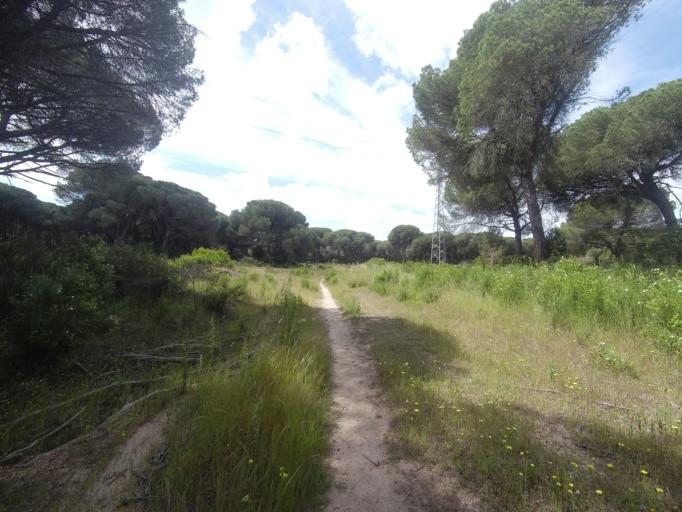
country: ES
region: Andalusia
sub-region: Provincia de Huelva
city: Aljaraque
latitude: 37.2249
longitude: -7.0689
